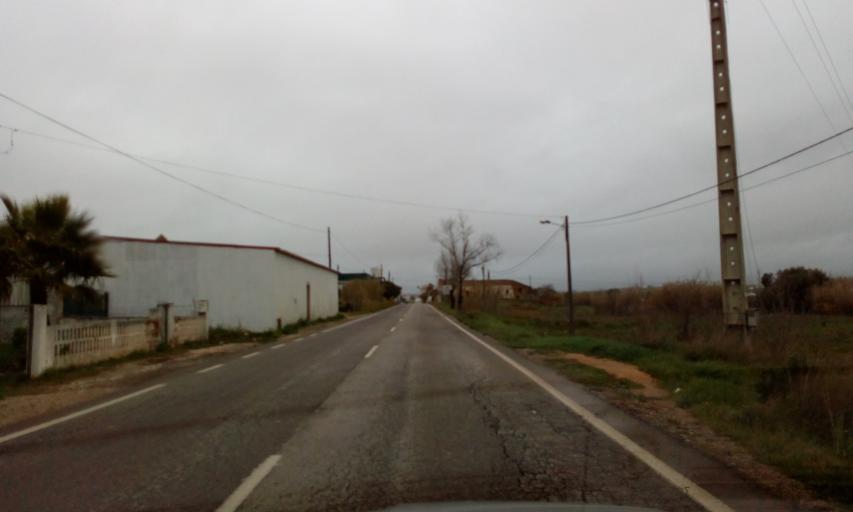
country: PT
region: Faro
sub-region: Albufeira
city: Guia
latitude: 37.1564
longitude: -8.2875
